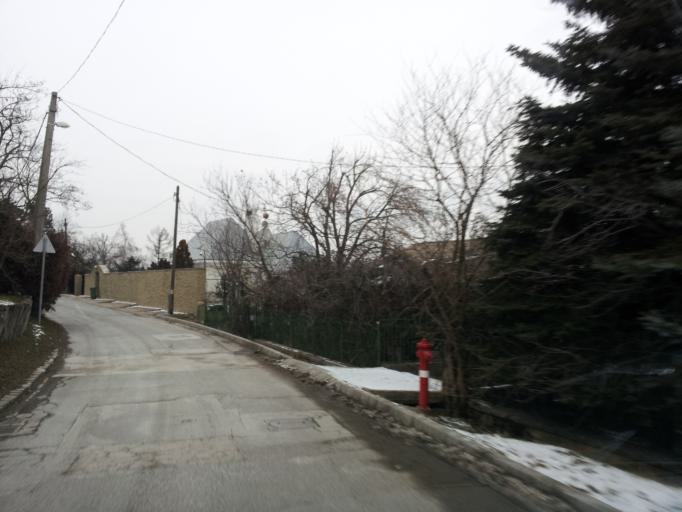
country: HU
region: Budapest
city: Budapest XII. keruelet
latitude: 47.4909
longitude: 18.9898
